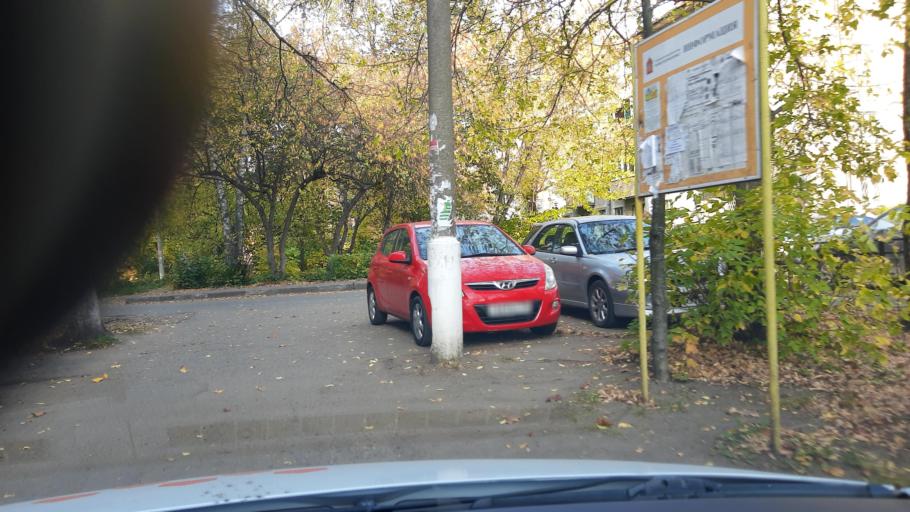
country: RU
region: Moskovskaya
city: Elektrostal'
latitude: 55.8012
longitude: 38.4393
